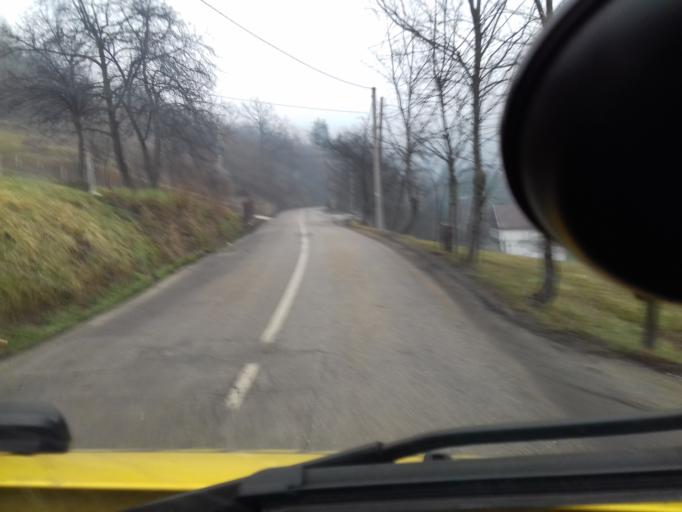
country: BA
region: Federation of Bosnia and Herzegovina
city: Lokvine
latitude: 44.1970
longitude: 17.8730
